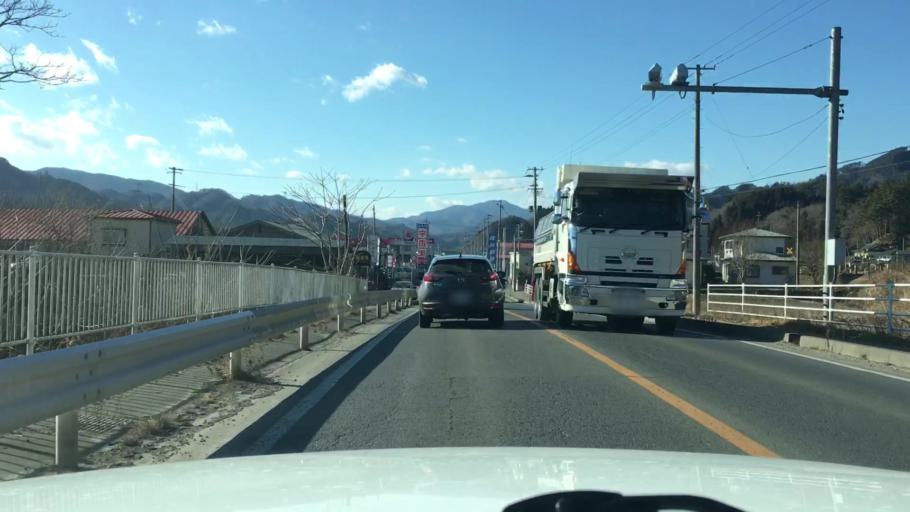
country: JP
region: Iwate
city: Miyako
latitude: 39.6327
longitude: 141.9000
